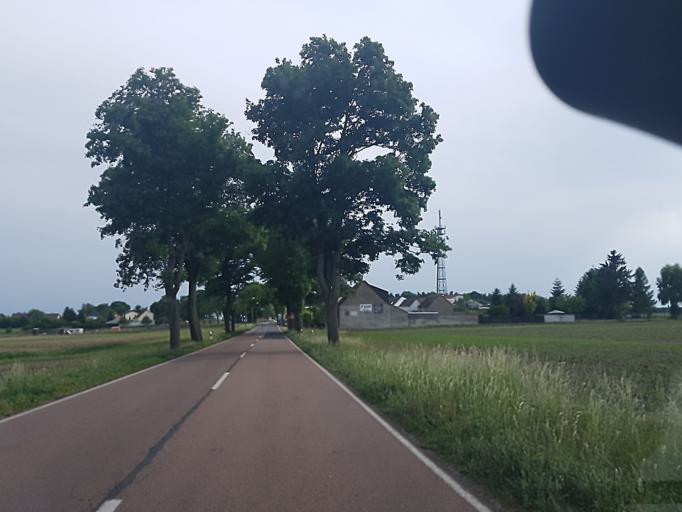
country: DE
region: Saxony-Anhalt
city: Nudersdorf
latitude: 51.9133
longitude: 12.6064
